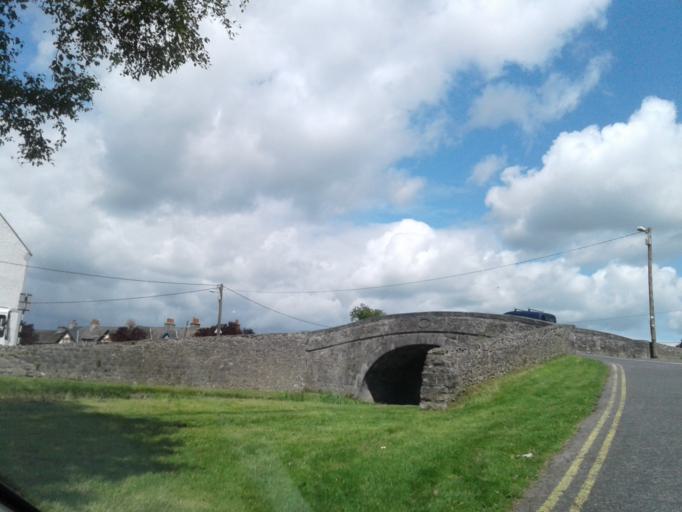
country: IE
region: Leinster
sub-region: Uibh Fhaili
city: Tullamore
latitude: 53.2775
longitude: -7.4866
